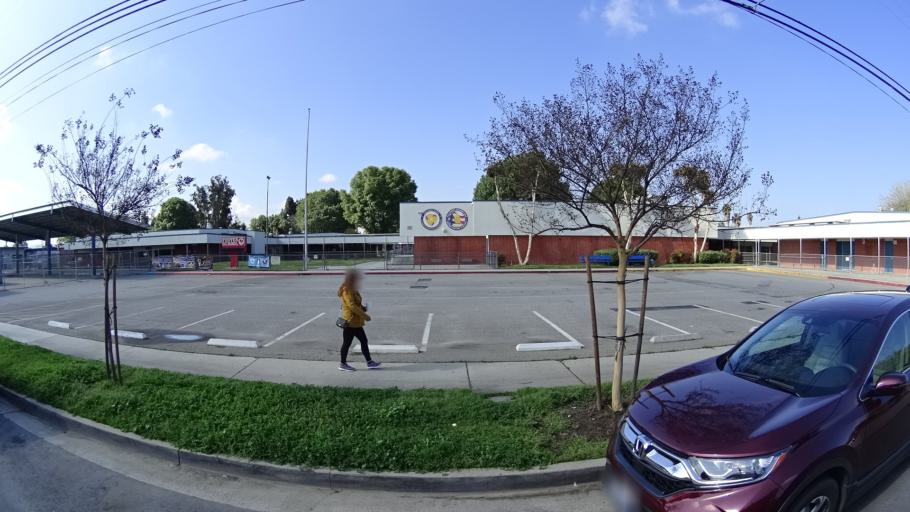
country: US
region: California
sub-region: Los Angeles County
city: Baldwin Park
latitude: 34.0719
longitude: -117.9718
